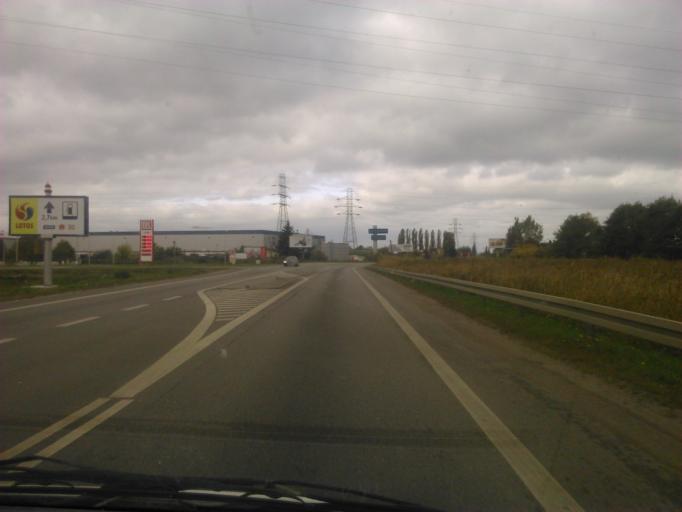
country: PL
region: Pomeranian Voivodeship
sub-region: Gdansk
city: Gdansk
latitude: 54.3443
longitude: 18.7211
